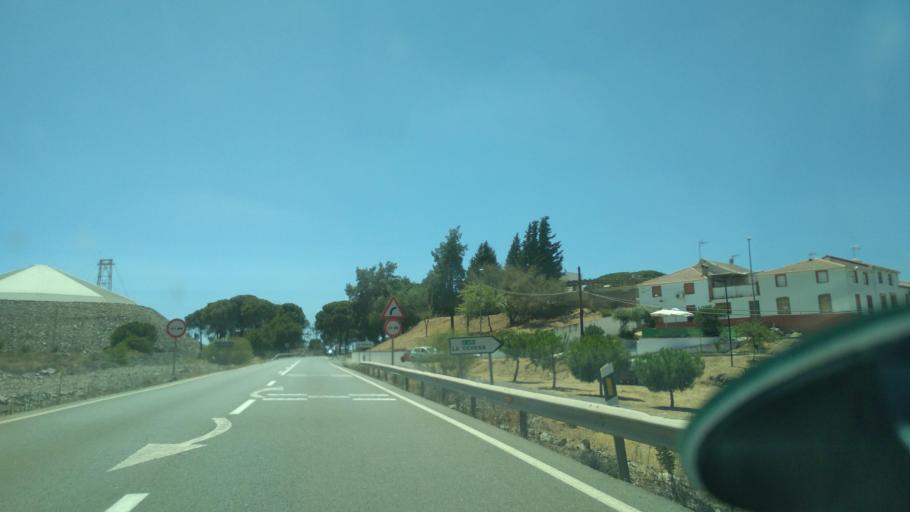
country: ES
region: Andalusia
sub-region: Provincia de Huelva
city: Nerva
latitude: 37.7145
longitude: -6.5799
